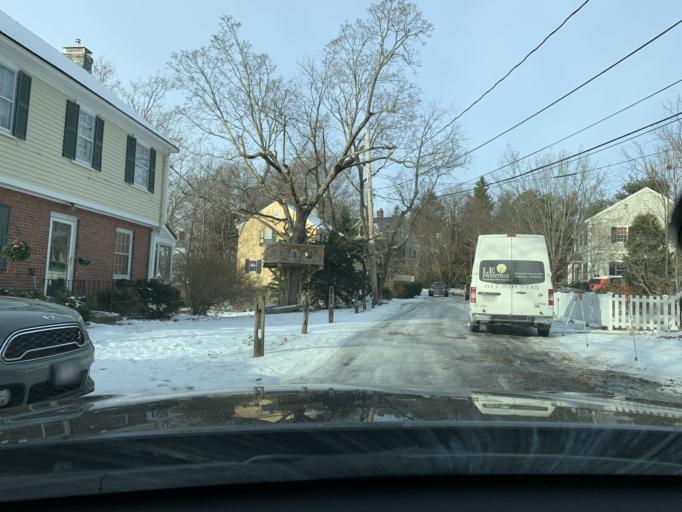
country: US
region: Massachusetts
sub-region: Norfolk County
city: Brookline
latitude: 42.3268
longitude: -71.1199
